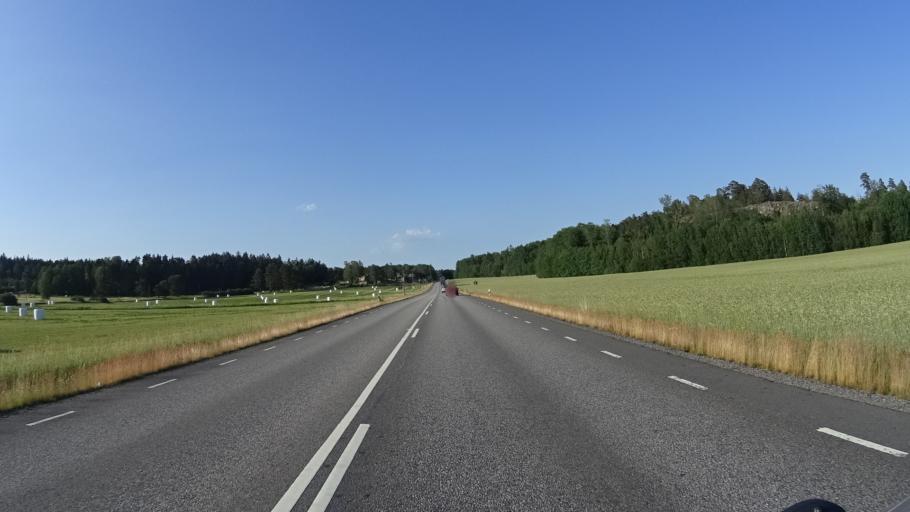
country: SE
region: Stockholm
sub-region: Sodertalje Kommun
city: Pershagen
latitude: 59.0903
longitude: 17.6147
